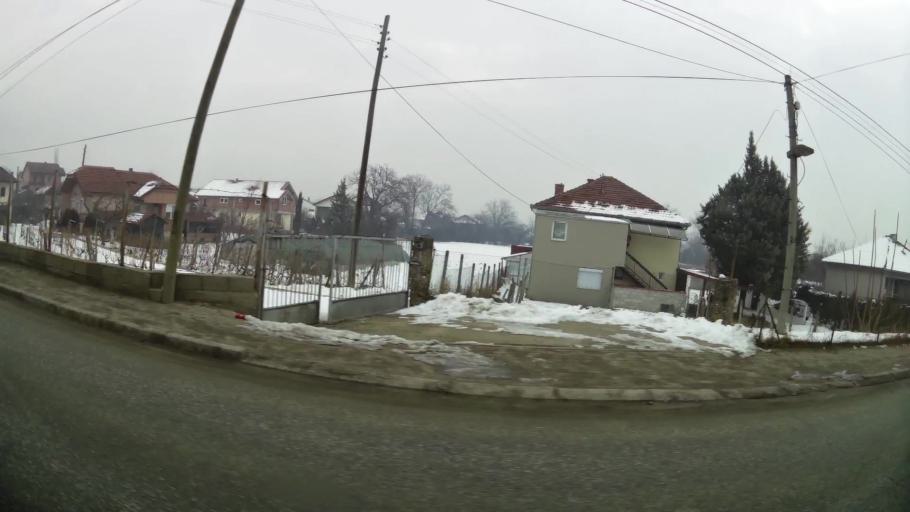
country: MK
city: Kondovo
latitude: 42.0441
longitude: 21.3464
